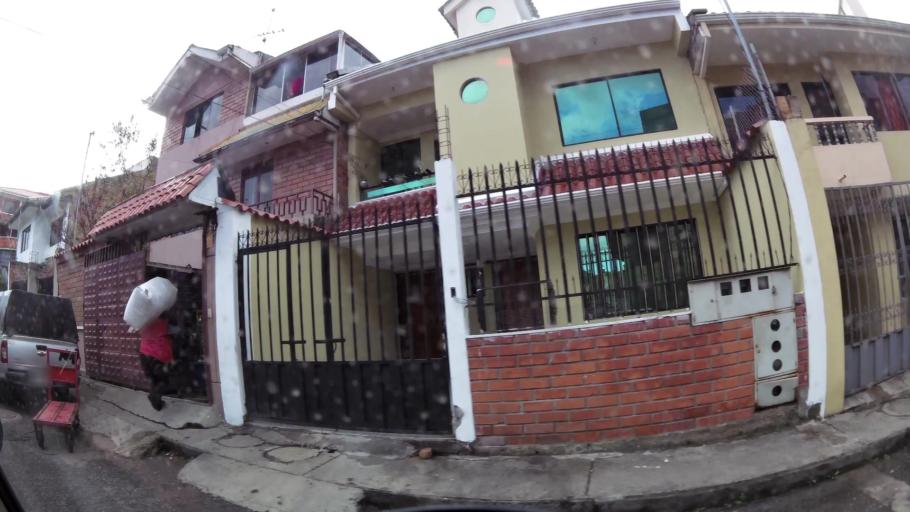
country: EC
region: Azuay
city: Cuenca
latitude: -2.9008
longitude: -79.0261
